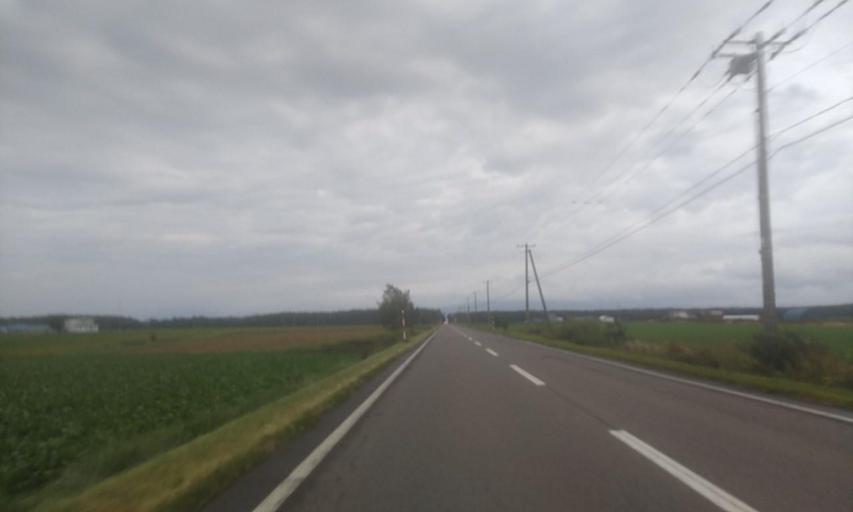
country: JP
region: Hokkaido
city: Abashiri
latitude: 43.8937
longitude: 144.5164
